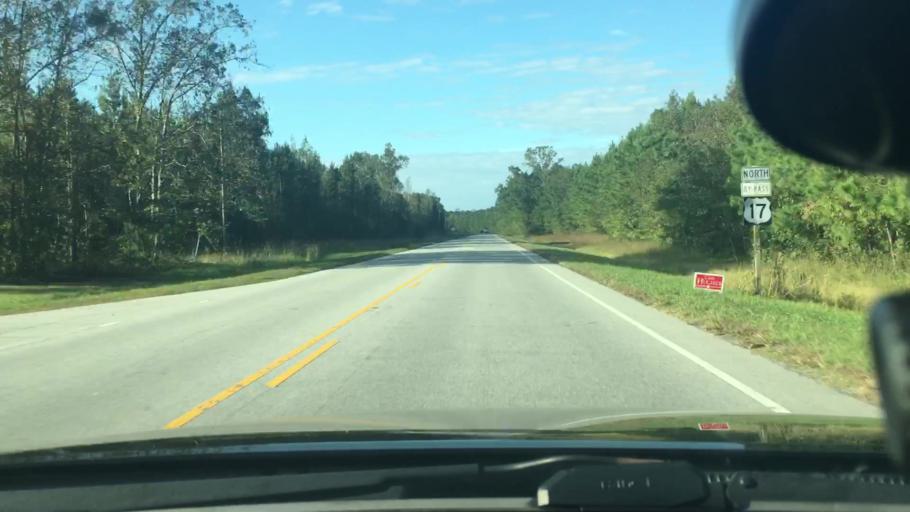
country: US
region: North Carolina
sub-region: Craven County
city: Vanceboro
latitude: 35.2953
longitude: -77.1306
